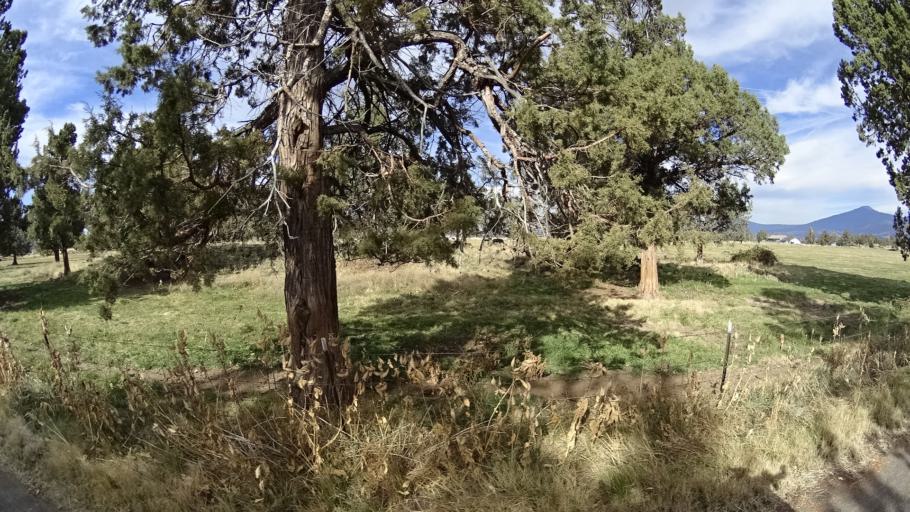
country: US
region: California
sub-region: Siskiyou County
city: Montague
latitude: 41.6096
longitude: -122.4029
